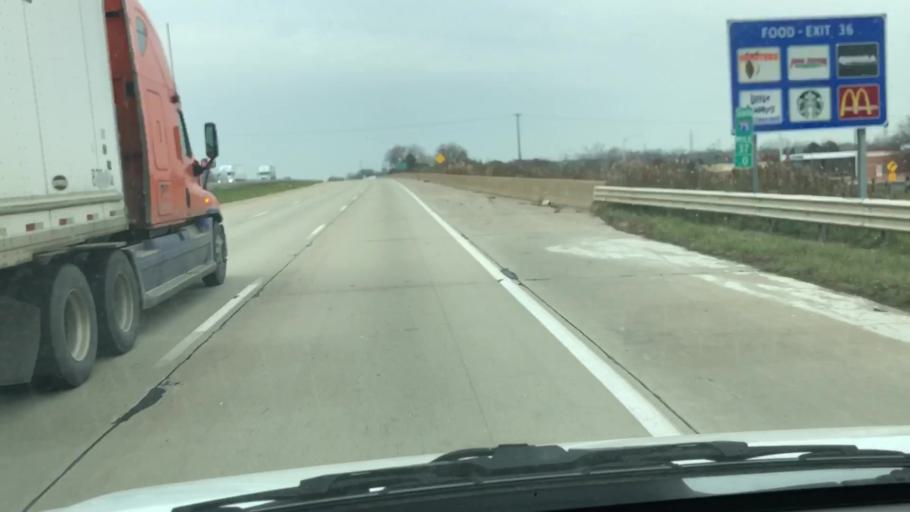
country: US
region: Michigan
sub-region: Wayne County
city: Southgate
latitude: 42.2104
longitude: -83.2264
